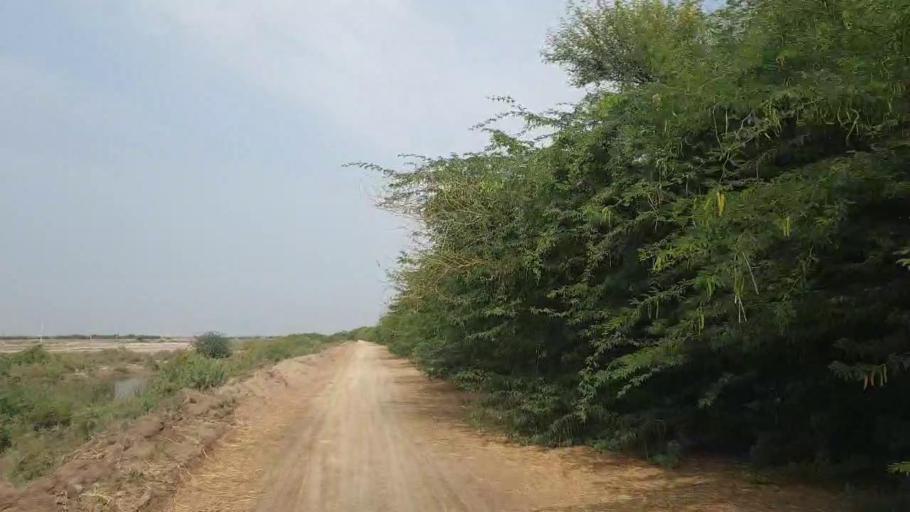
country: PK
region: Sindh
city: Badin
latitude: 24.5568
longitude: 68.7318
